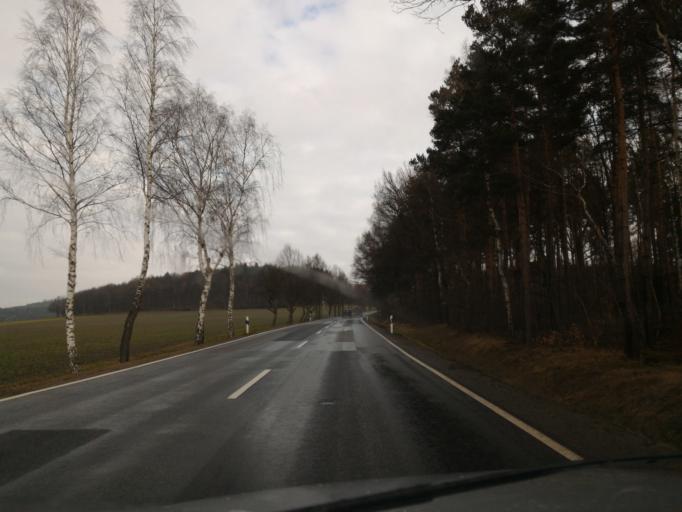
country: DE
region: Saxony
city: Grossschonau
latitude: 50.9122
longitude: 14.6611
